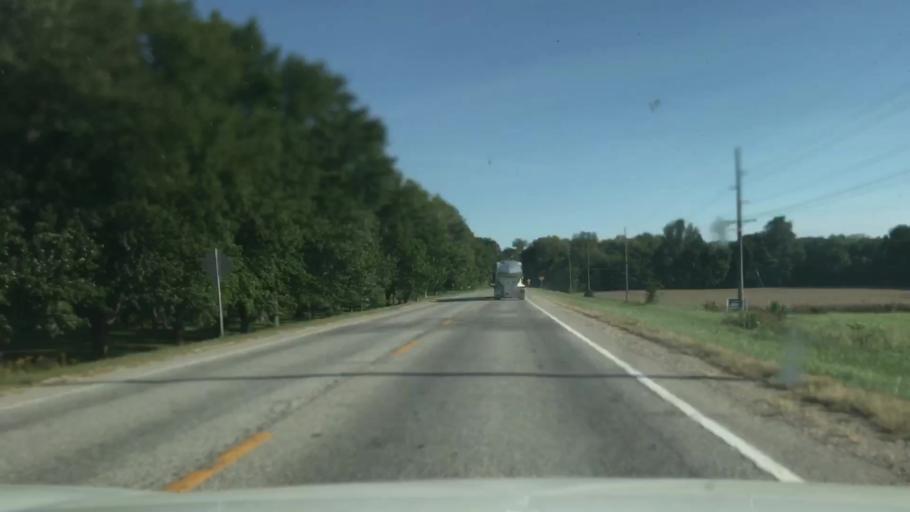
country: US
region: Illinois
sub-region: Adams County
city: Quincy
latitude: 39.8465
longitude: -91.3756
